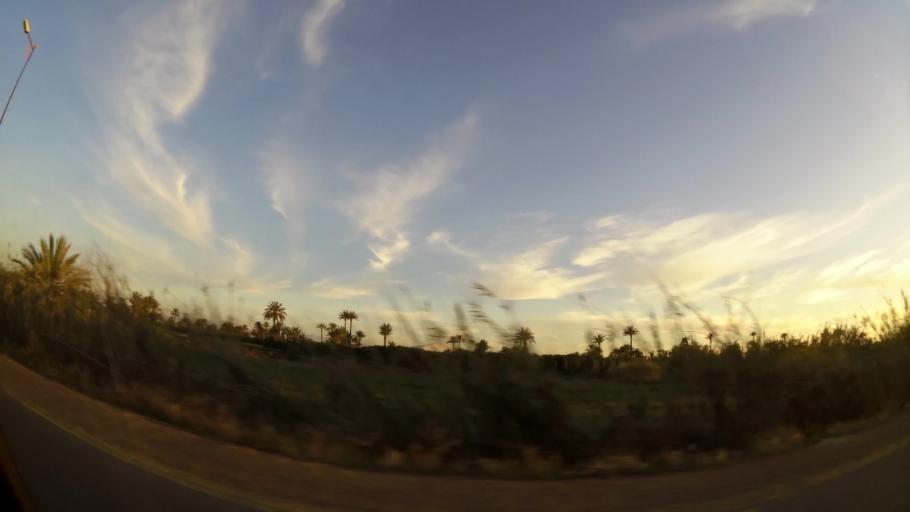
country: MA
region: Marrakech-Tensift-Al Haouz
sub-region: Marrakech
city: Marrakesh
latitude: 31.6902
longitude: -8.0112
